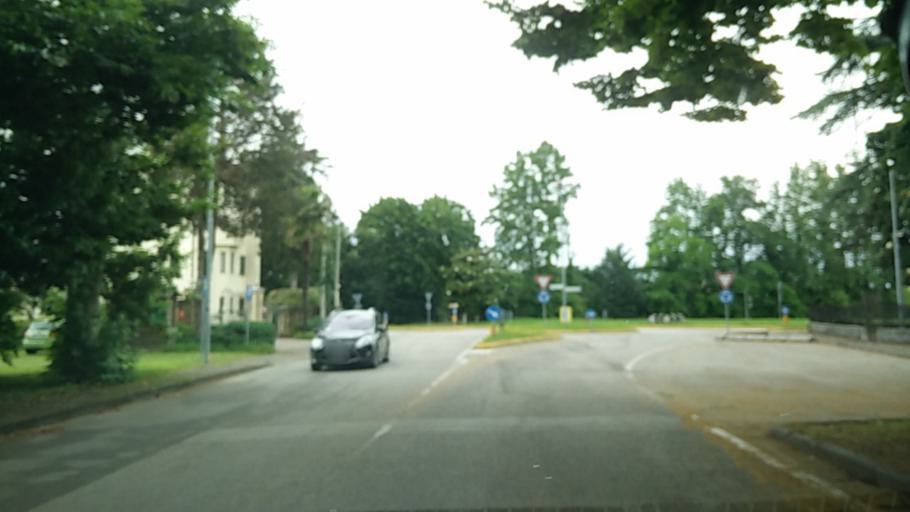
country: IT
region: Veneto
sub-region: Provincia di Treviso
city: Mareno di Piave
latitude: 45.8437
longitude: 12.3648
